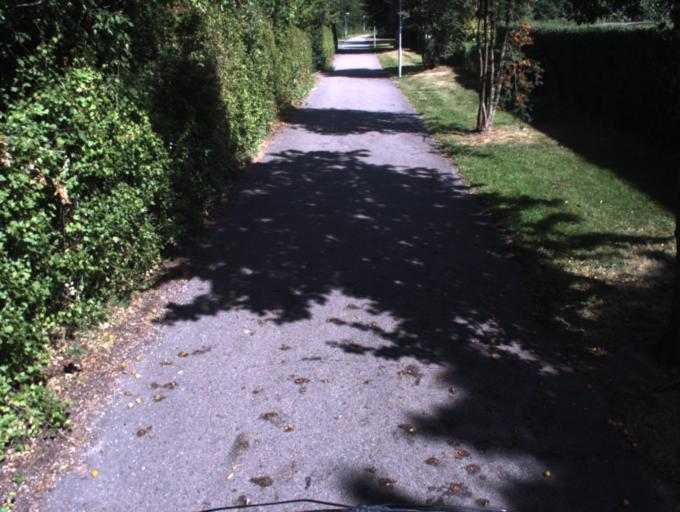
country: SE
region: Skane
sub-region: Helsingborg
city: Barslov
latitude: 56.0078
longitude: 12.7991
